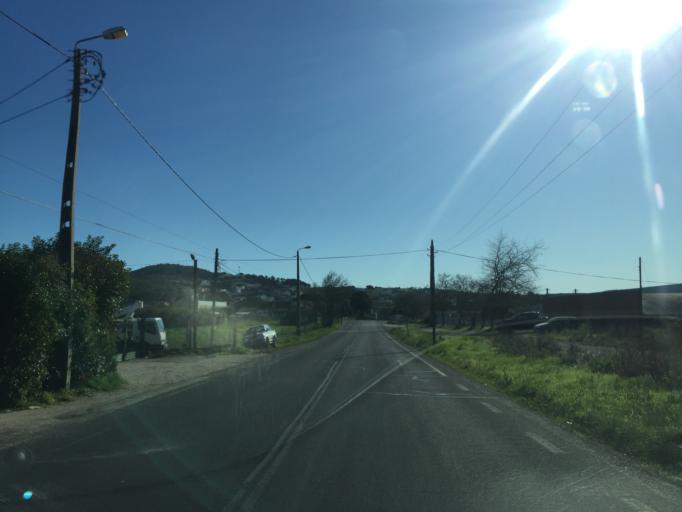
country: PT
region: Lisbon
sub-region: Sintra
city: Pero Pinheiro
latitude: 38.8311
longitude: -9.3052
